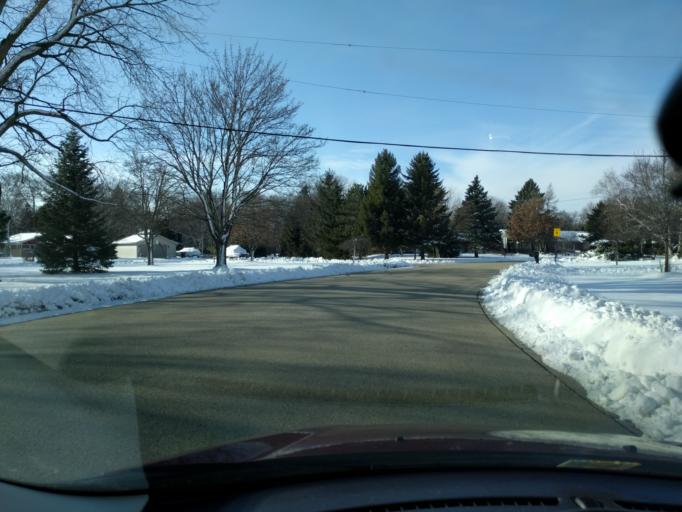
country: US
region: Wisconsin
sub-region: Milwaukee County
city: Glendale
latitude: 43.1261
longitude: -87.9216
